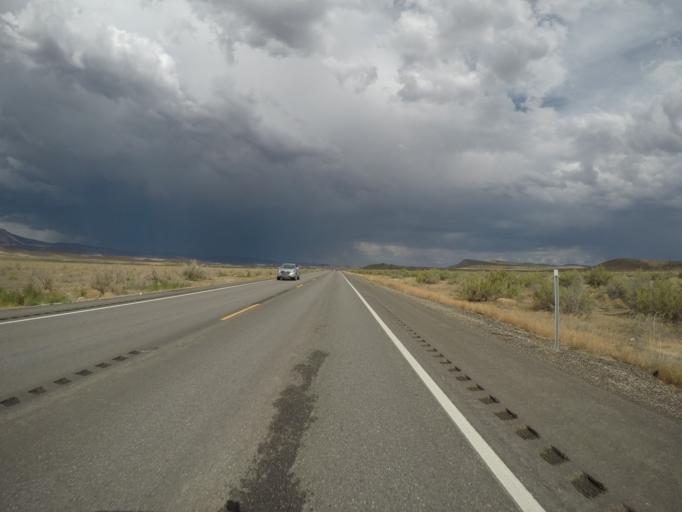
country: US
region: Utah
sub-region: Uintah County
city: Naples
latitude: 40.2921
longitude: -109.1702
